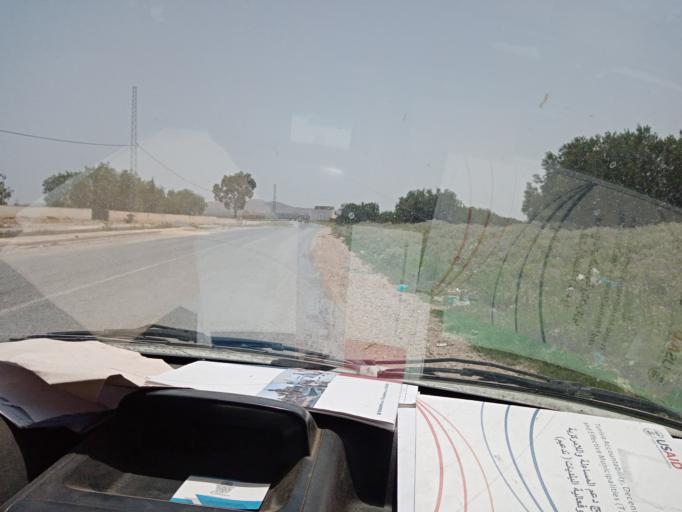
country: TN
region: Al Qayrawan
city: Sbikha
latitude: 36.1146
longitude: 10.0978
